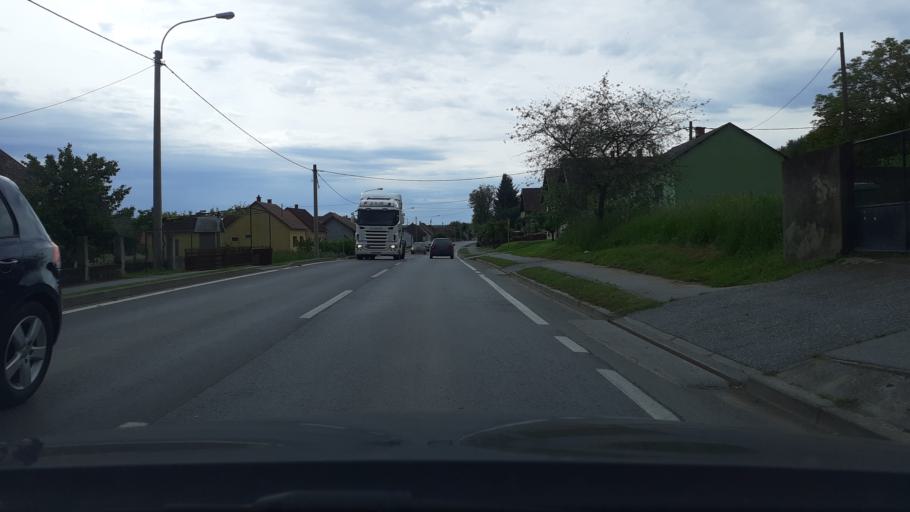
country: HR
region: Pozesko-Slavonska
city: Pleternica
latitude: 45.2994
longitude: 17.7936
